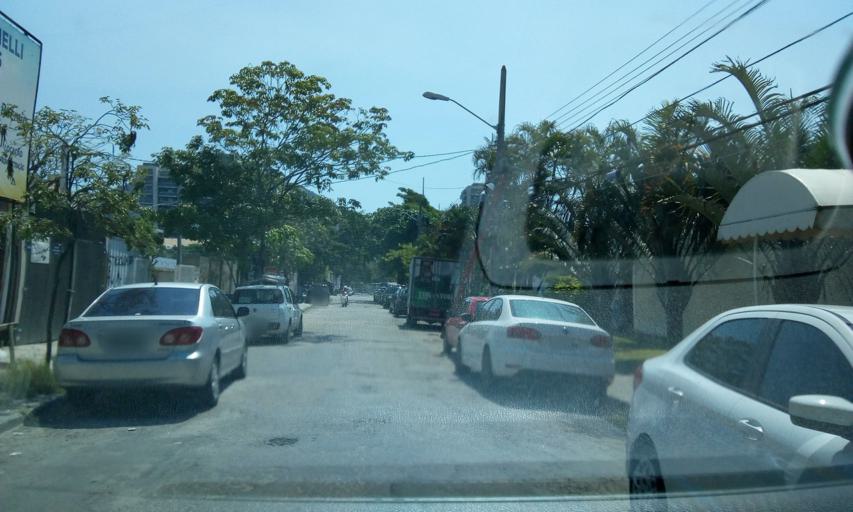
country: BR
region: Rio de Janeiro
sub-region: Nilopolis
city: Nilopolis
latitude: -23.0231
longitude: -43.4810
